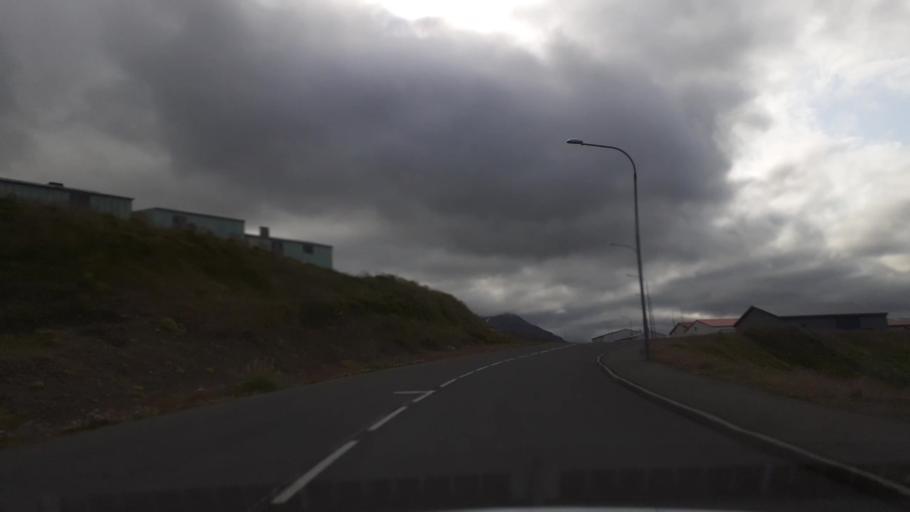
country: IS
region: Northeast
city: Akureyri
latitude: 65.9538
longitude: -18.1820
